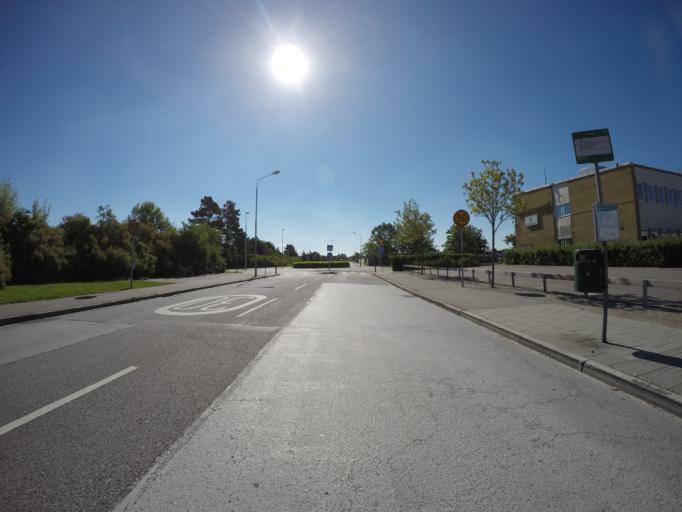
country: SE
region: Skane
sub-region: Burlovs Kommun
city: Arloev
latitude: 55.5912
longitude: 13.0709
